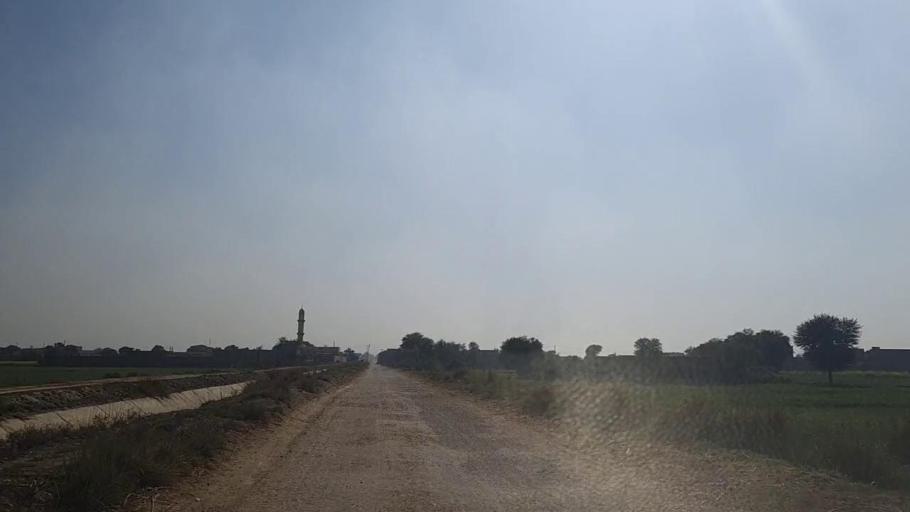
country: PK
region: Sindh
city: Shahpur Chakar
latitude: 26.1915
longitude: 68.5835
